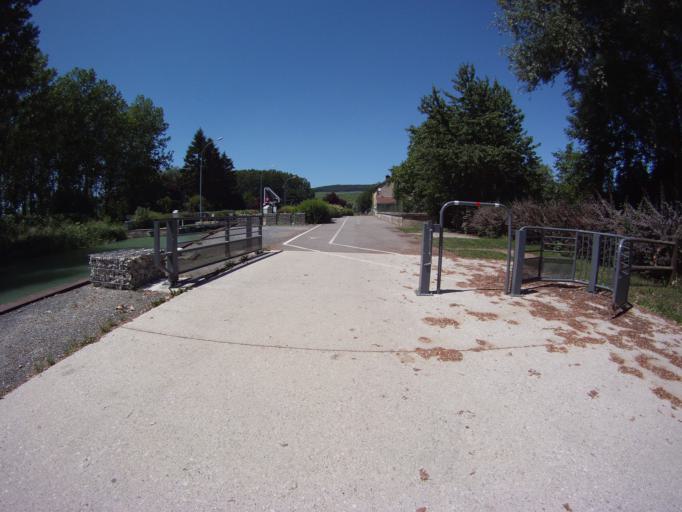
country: FR
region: Champagne-Ardenne
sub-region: Departement de la Marne
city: Epernay
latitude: 49.0700
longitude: 3.9448
